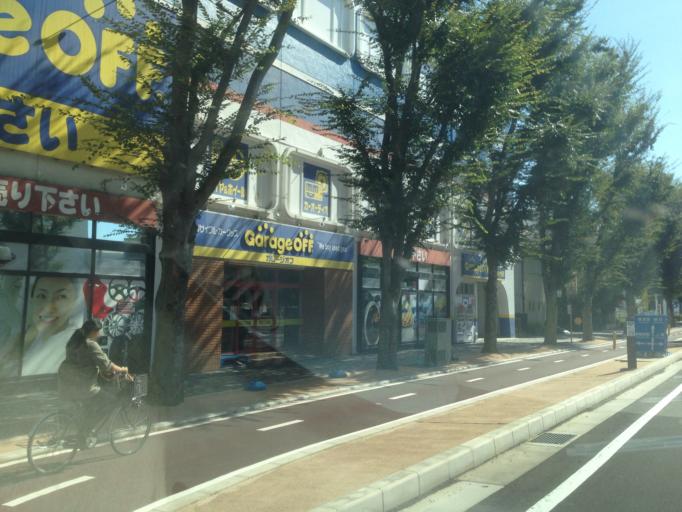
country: JP
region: Tokyo
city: Hachioji
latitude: 35.5769
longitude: 139.3657
